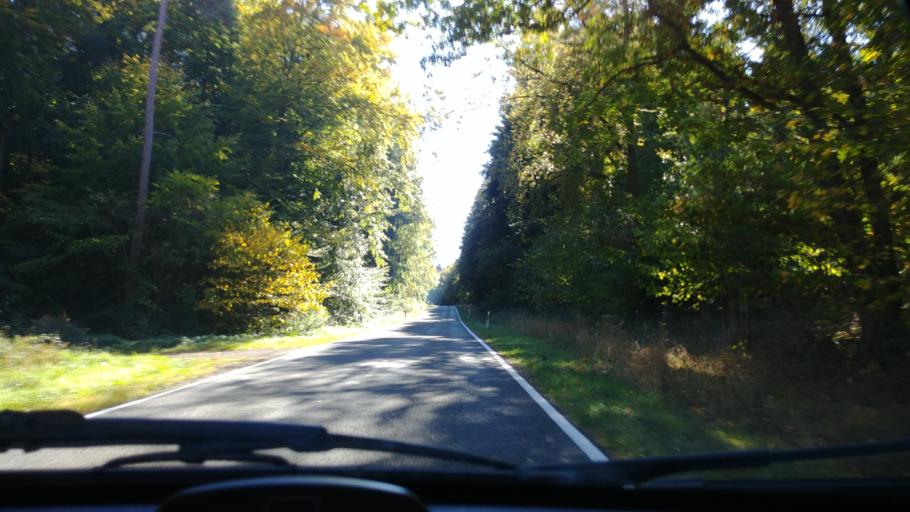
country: DE
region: Hesse
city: Burg Hohenstein
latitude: 50.1783
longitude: 8.1026
